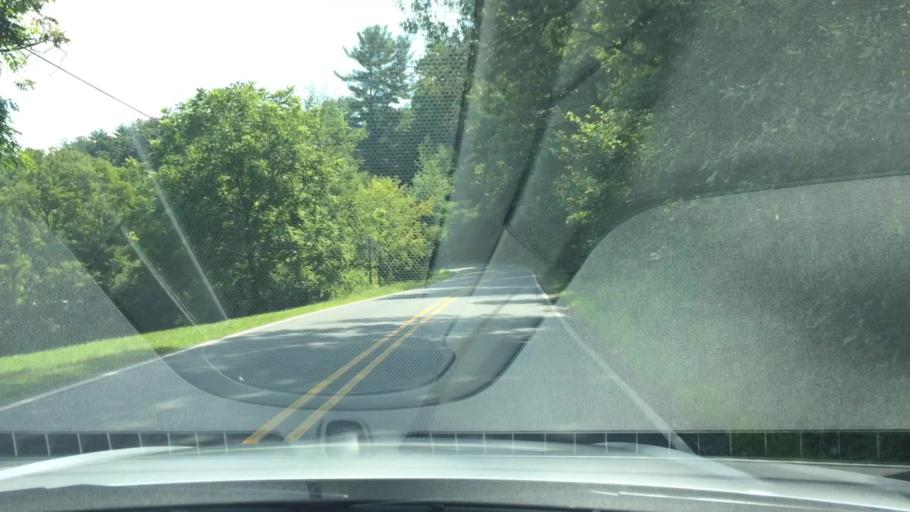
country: US
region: North Carolina
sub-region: Buncombe County
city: Weaverville
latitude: 35.6805
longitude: -82.5892
